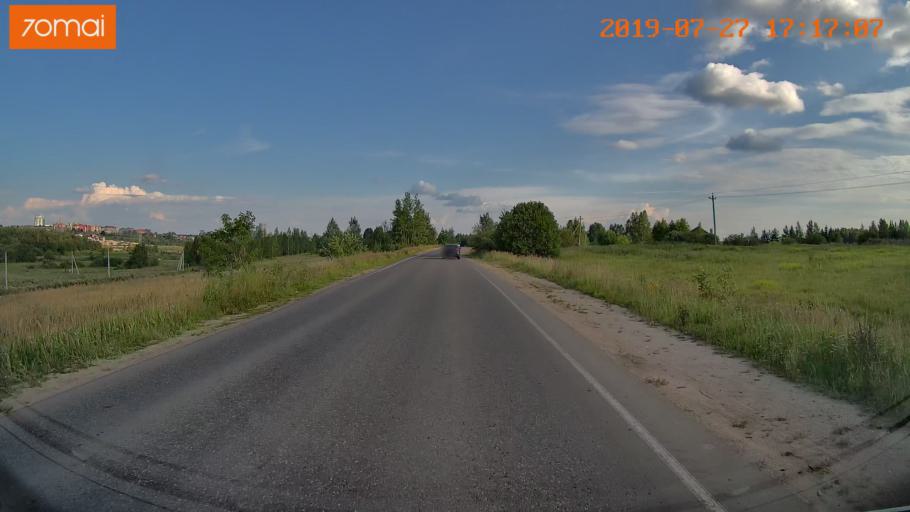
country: RU
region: Ivanovo
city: Novo-Talitsy
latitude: 57.0402
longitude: 40.8918
